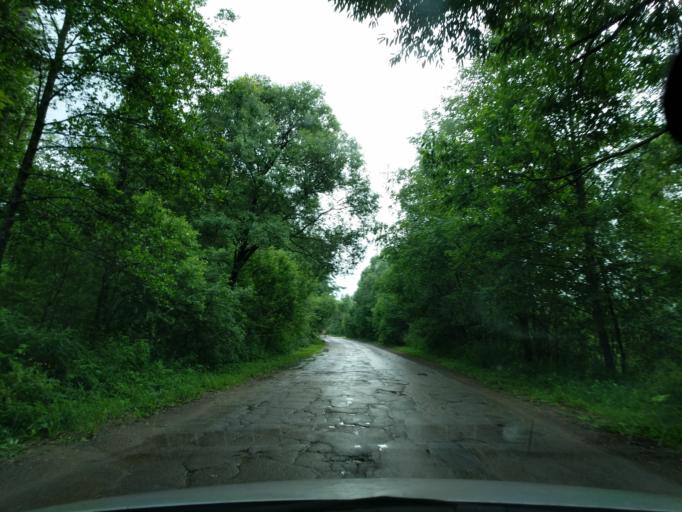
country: RU
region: Kaluga
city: Nikola-Lenivets
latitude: 54.7684
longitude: 35.7098
